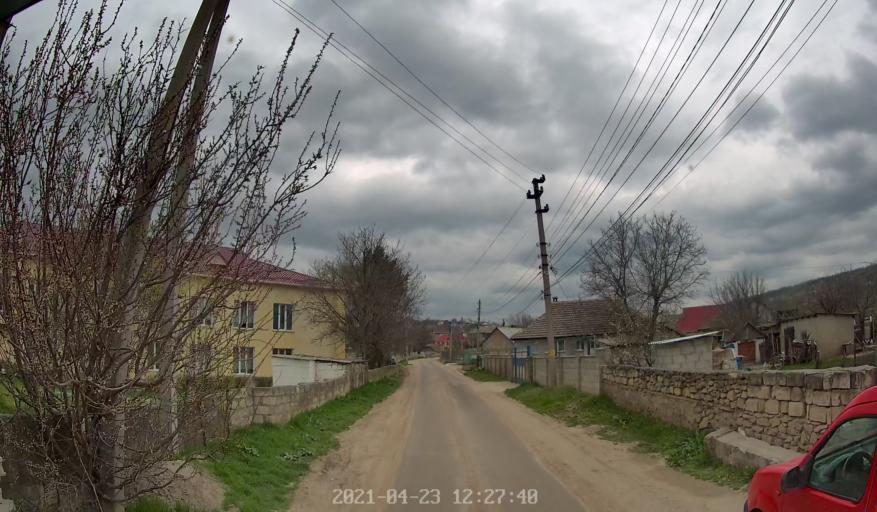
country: MD
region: Chisinau
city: Vadul lui Voda
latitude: 47.1249
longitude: 29.0007
